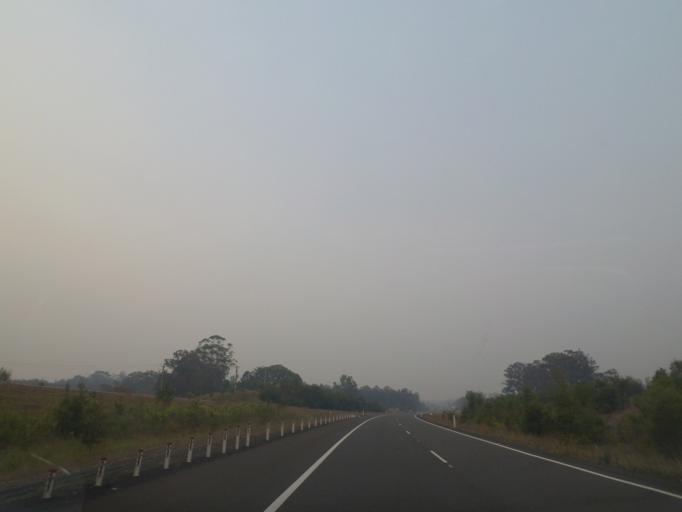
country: AU
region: New South Wales
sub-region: Nambucca Shire
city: Macksville
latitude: -30.7317
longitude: 152.9214
